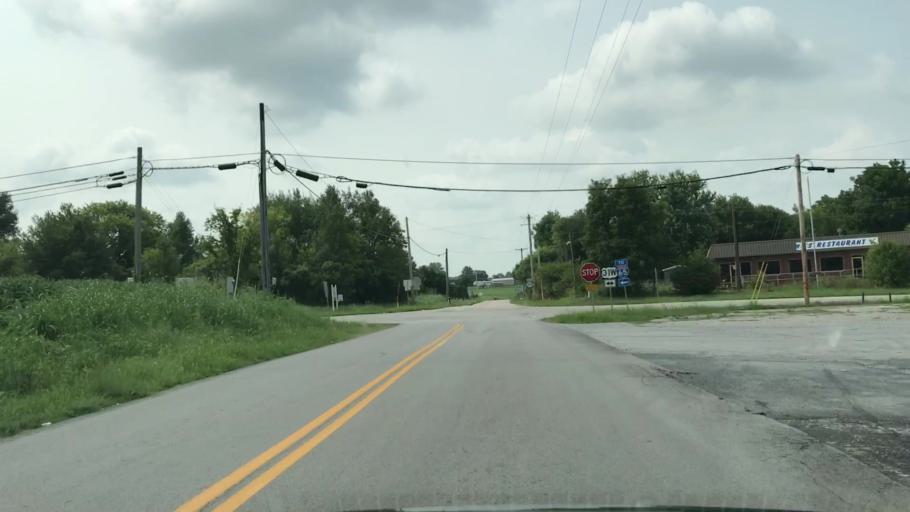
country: US
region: Kentucky
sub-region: Edmonson County
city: Brownsville
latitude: 37.0928
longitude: -86.1475
